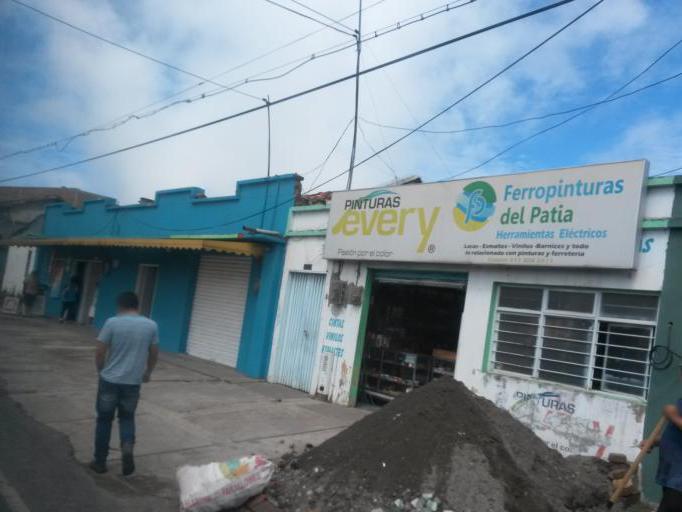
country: CO
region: Cauca
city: El Bordo
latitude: 2.1167
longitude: -76.9844
